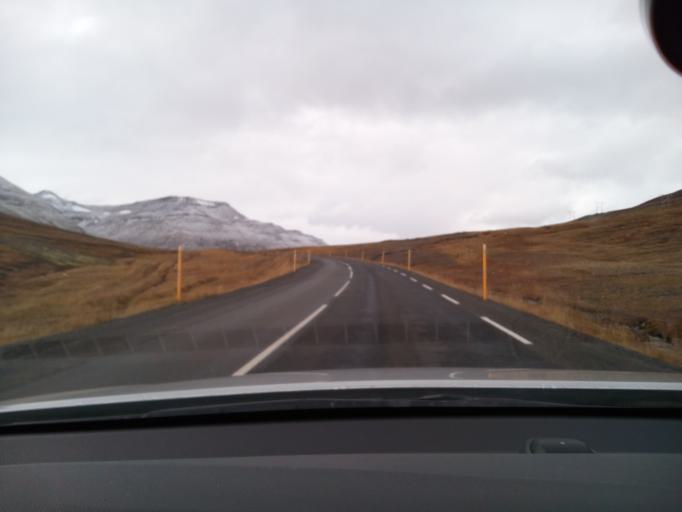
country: IS
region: Northeast
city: Dalvik
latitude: 65.4713
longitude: -18.6801
